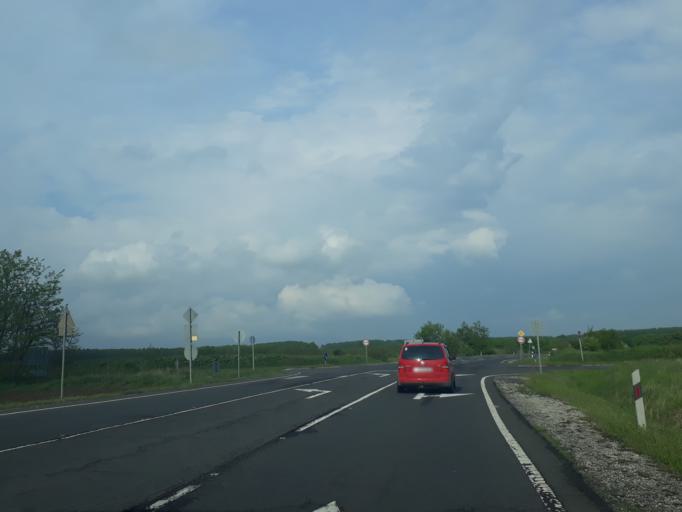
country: HU
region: Szabolcs-Szatmar-Bereg
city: Demecser
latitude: 48.0664
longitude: 21.9330
